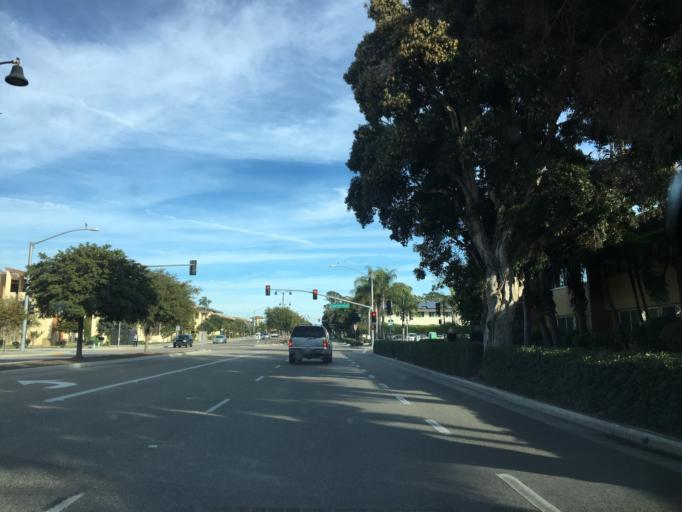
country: US
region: California
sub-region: Santa Barbara County
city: Isla Vista
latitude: 34.4173
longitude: -119.8578
